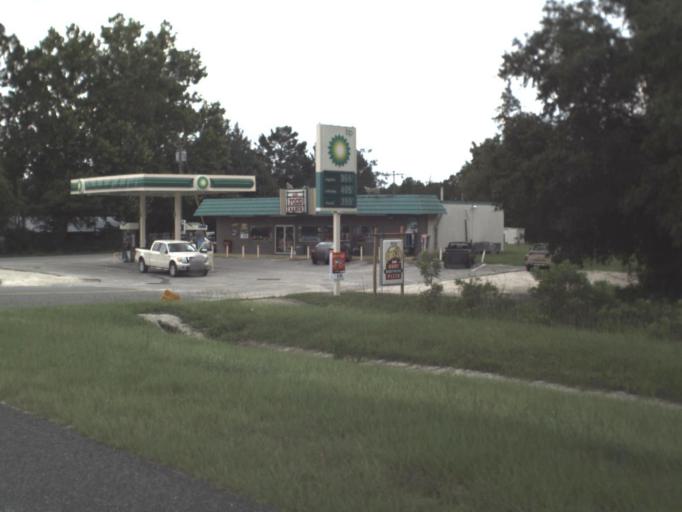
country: US
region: Florida
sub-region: Levy County
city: East Bronson
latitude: 29.4108
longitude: -82.5405
